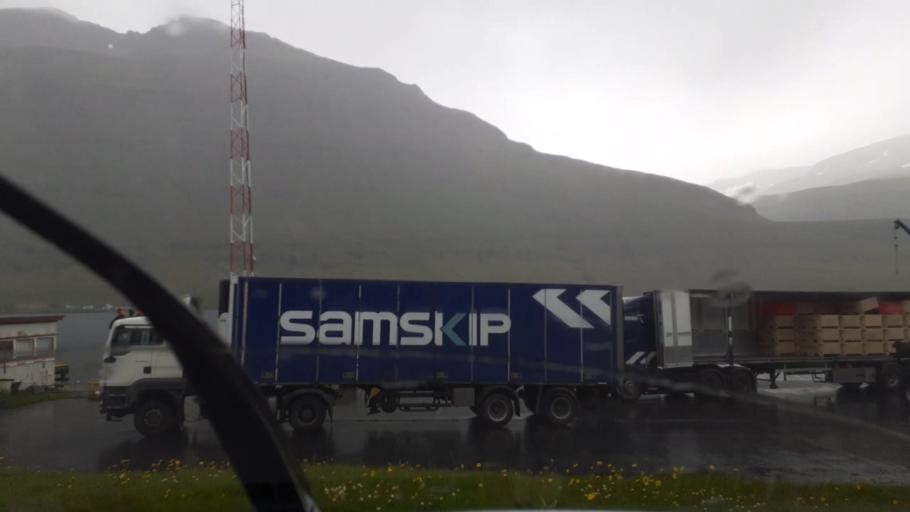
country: IS
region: East
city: Eskifjoerdur
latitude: 65.2663
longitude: -13.9915
